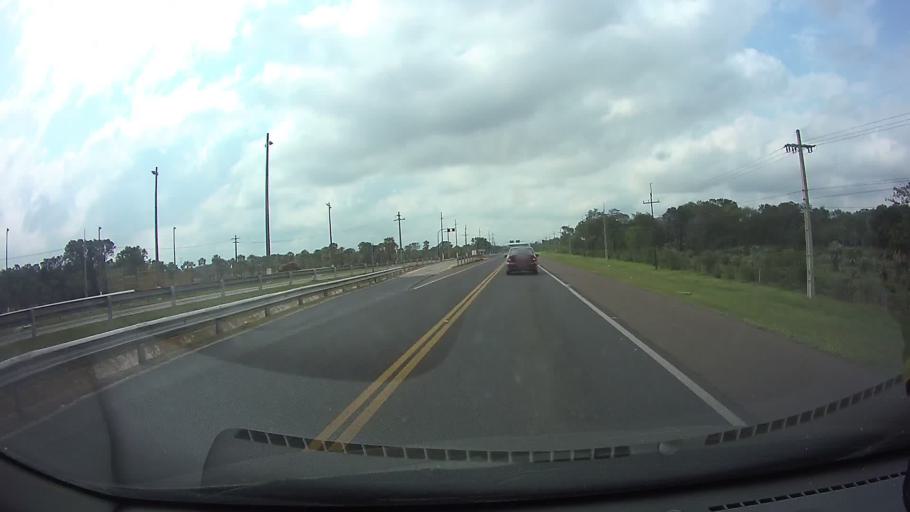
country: PY
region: Central
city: Limpio
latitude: -25.1217
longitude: -57.4341
